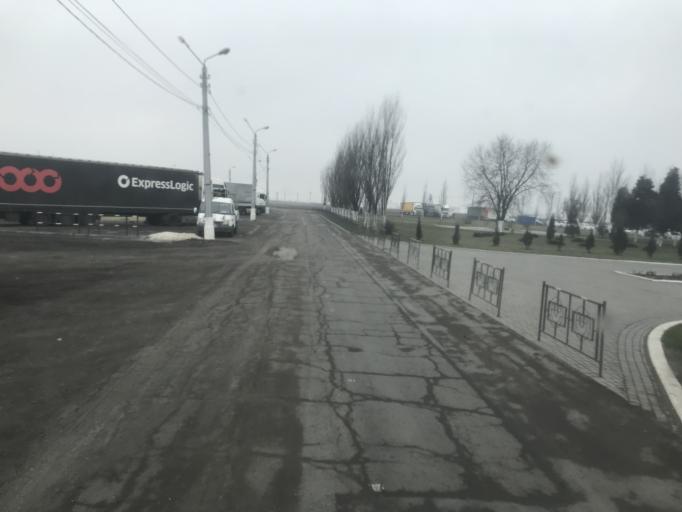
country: RU
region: Volgograd
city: Svetlyy Yar
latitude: 48.4901
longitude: 44.6626
